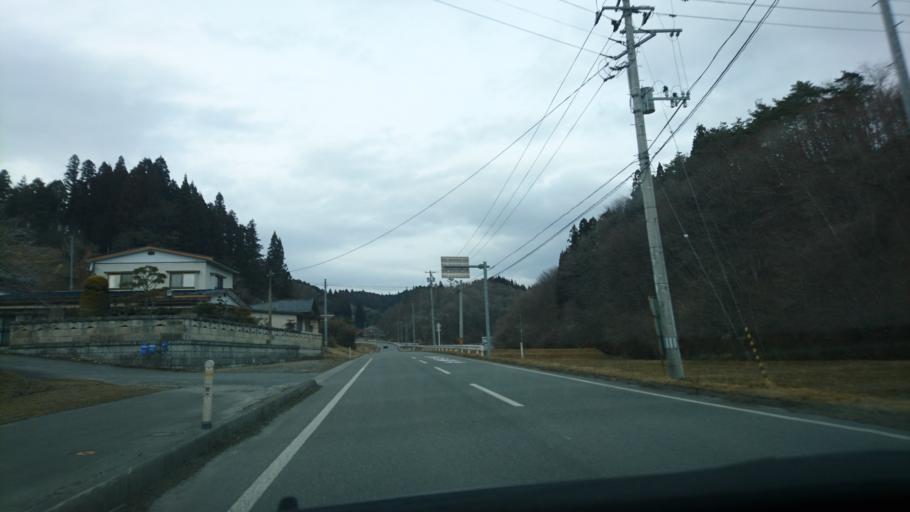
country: JP
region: Iwate
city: Ichinoseki
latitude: 38.9647
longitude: 141.3642
